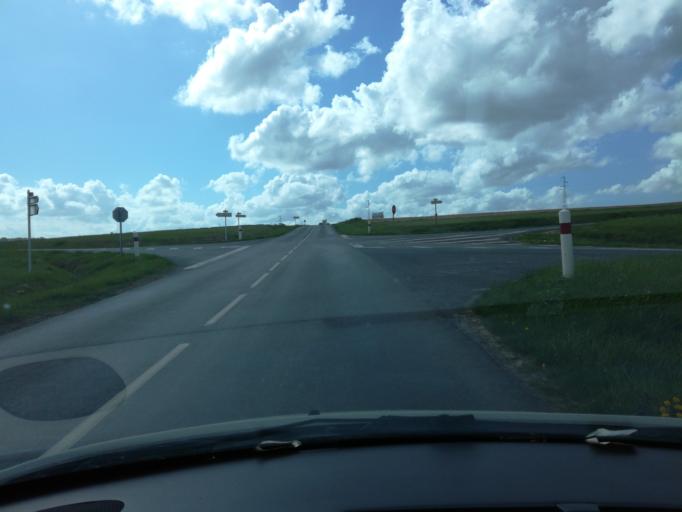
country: FR
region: Picardie
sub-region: Departement de la Somme
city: Quevauvillers
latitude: 49.8864
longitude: 2.0610
